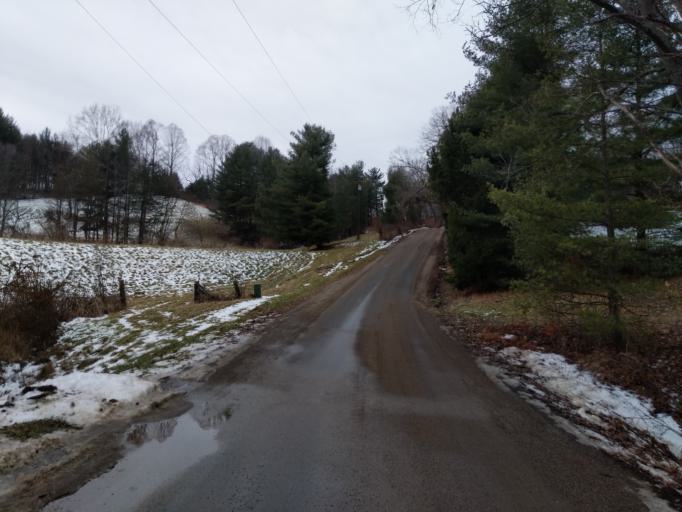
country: US
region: Ohio
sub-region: Athens County
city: The Plains
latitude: 39.3308
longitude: -82.1417
